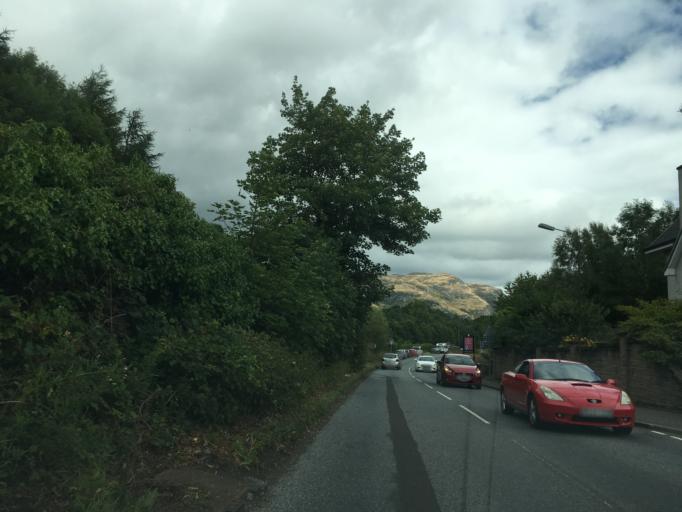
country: GB
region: Scotland
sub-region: Stirling
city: Stirling
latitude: 56.1403
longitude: -3.9204
